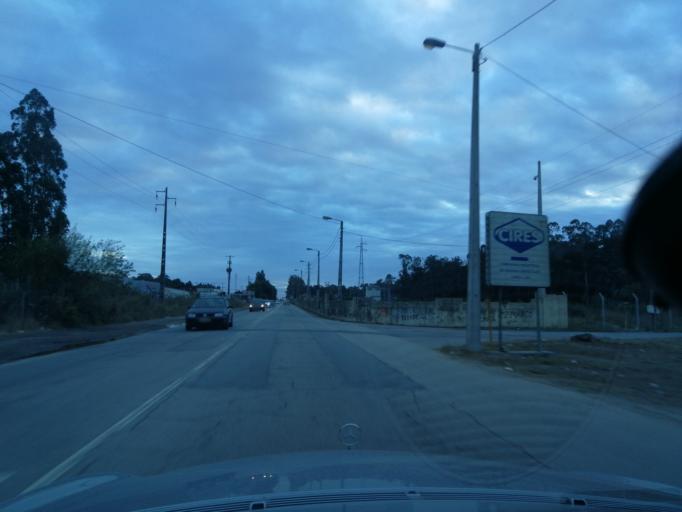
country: PT
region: Aveiro
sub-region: Estarreja
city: Beduido
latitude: 40.7800
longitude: -8.5663
